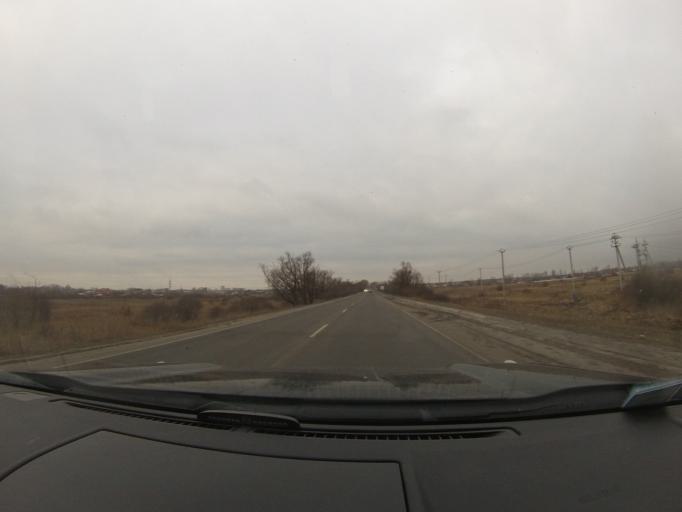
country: RU
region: Moskovskaya
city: Lopatinskiy
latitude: 55.3269
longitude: 38.7304
